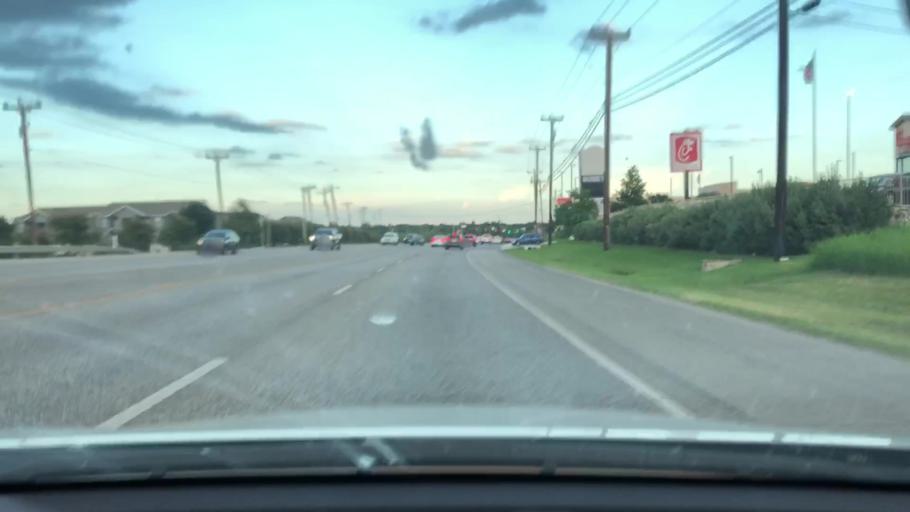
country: US
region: Texas
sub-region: Bexar County
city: Kirby
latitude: 29.4851
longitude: -98.3508
